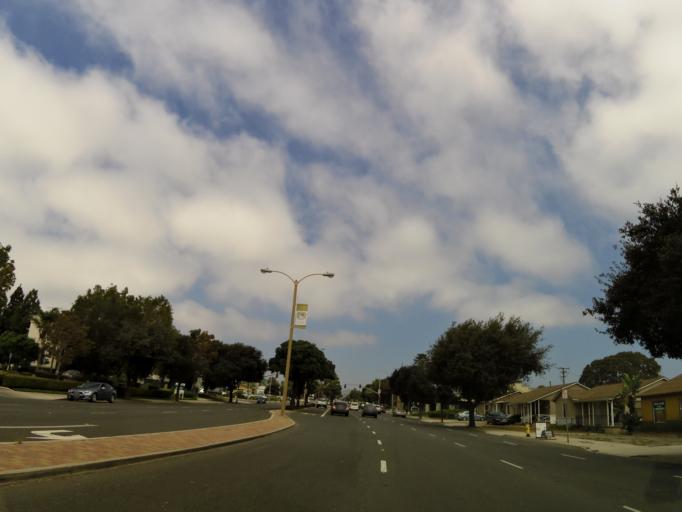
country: US
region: California
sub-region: Ventura County
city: El Rio
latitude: 34.2546
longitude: -119.2102
